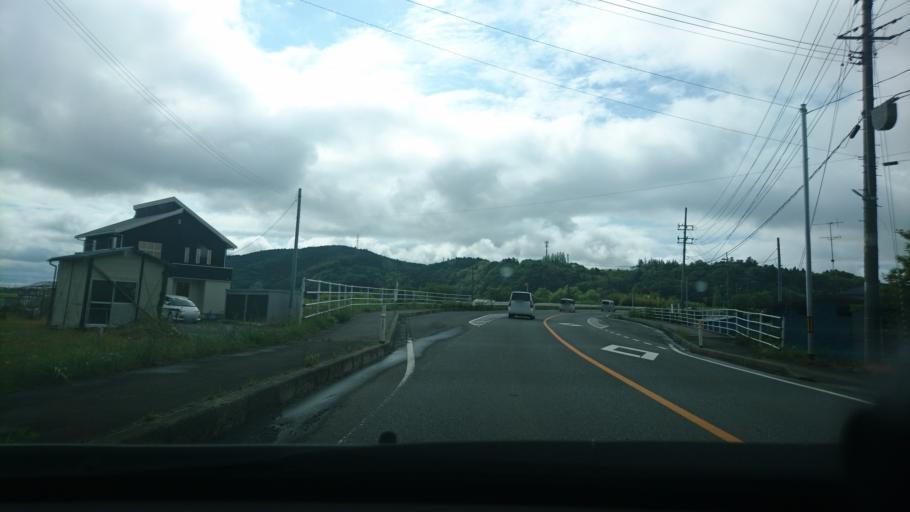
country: JP
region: Miyagi
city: Ishinomaki
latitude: 38.5059
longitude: 141.3120
